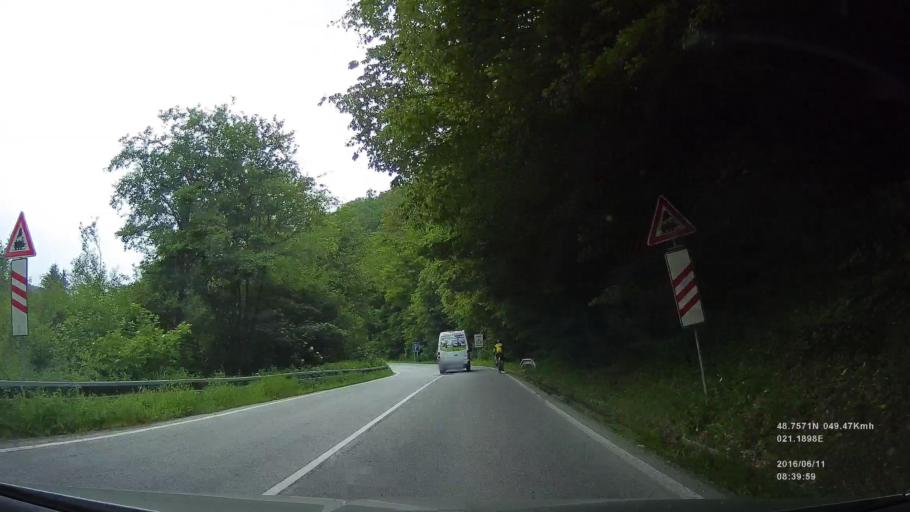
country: SK
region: Kosicky
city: Kosice
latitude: 48.7459
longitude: 21.2363
